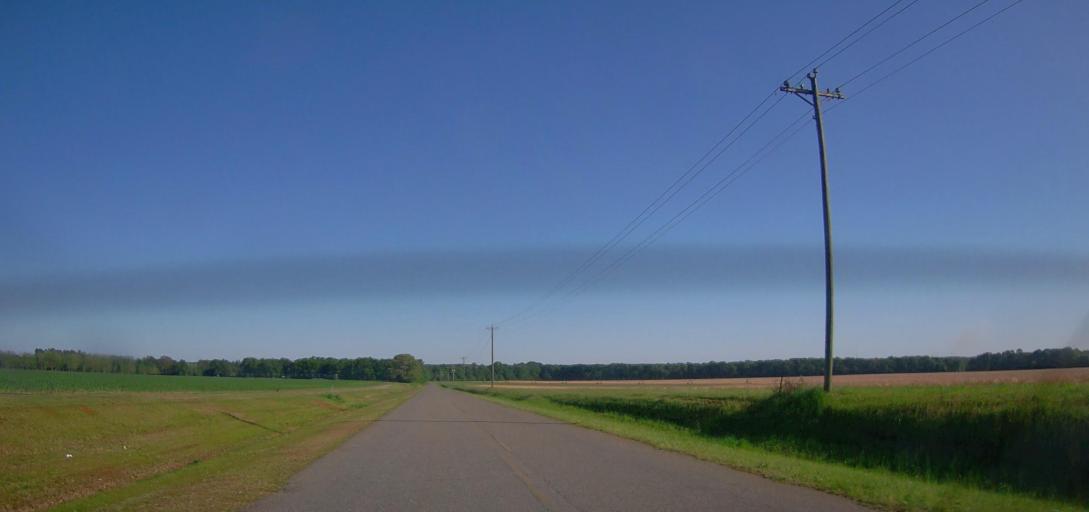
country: US
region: Georgia
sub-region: Houston County
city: Perry
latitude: 32.4266
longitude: -83.7800
